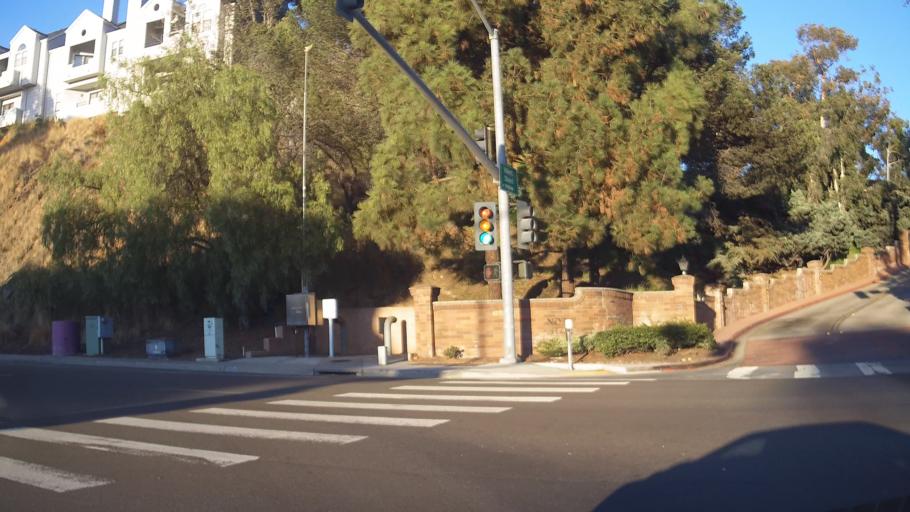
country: US
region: California
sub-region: San Diego County
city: Poway
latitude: 32.9138
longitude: -117.1101
